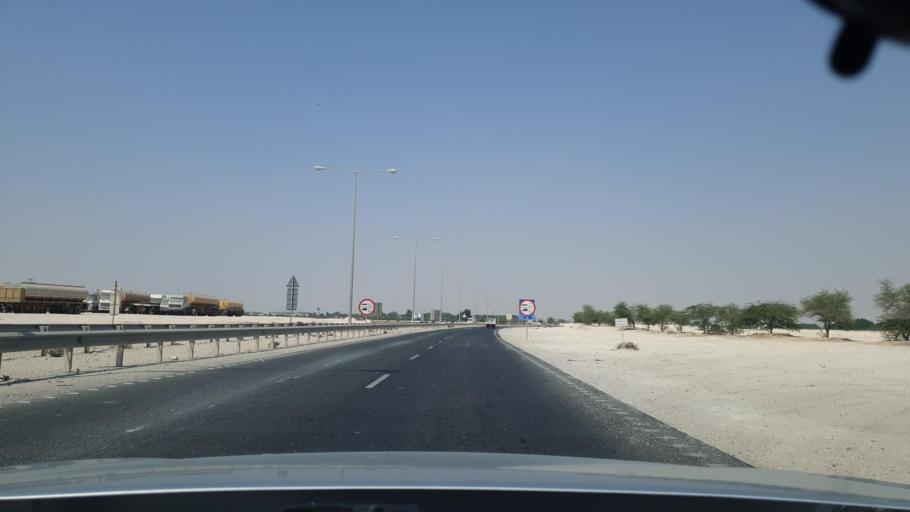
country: QA
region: Al Khawr
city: Al Khawr
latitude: 25.7221
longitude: 51.4991
